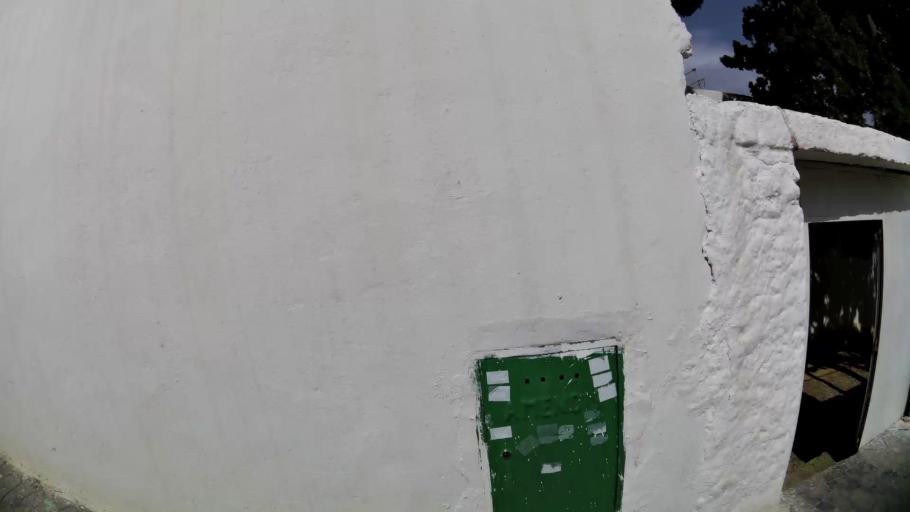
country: MA
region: Tanger-Tetouan
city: Tetouan
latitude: 35.5841
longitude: -5.3594
